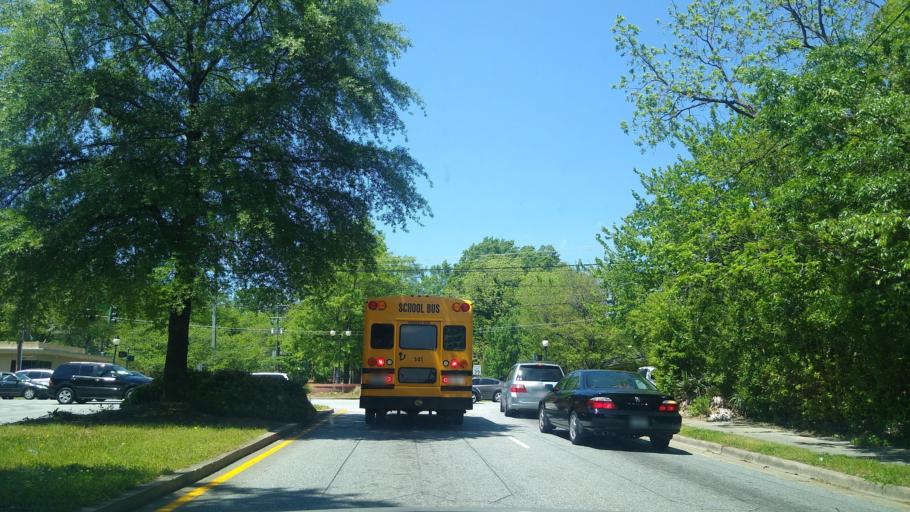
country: US
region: North Carolina
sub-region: Guilford County
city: Greensboro
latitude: 36.0806
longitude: -79.7800
